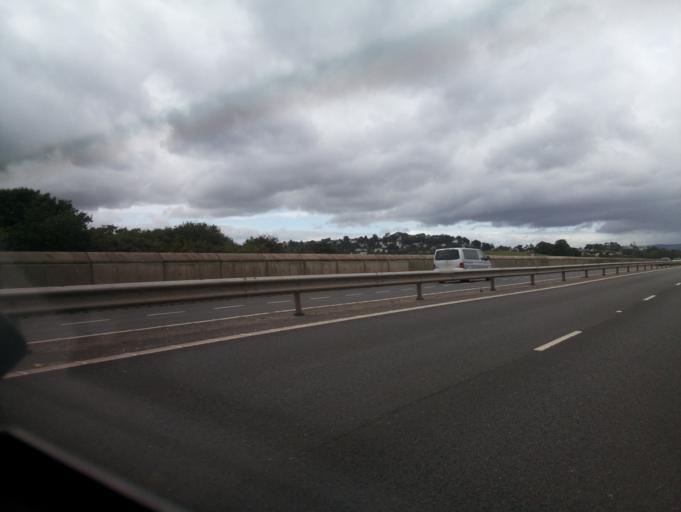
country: GB
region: England
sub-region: Devon
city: Kingskerswell
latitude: 50.5169
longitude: -3.5893
